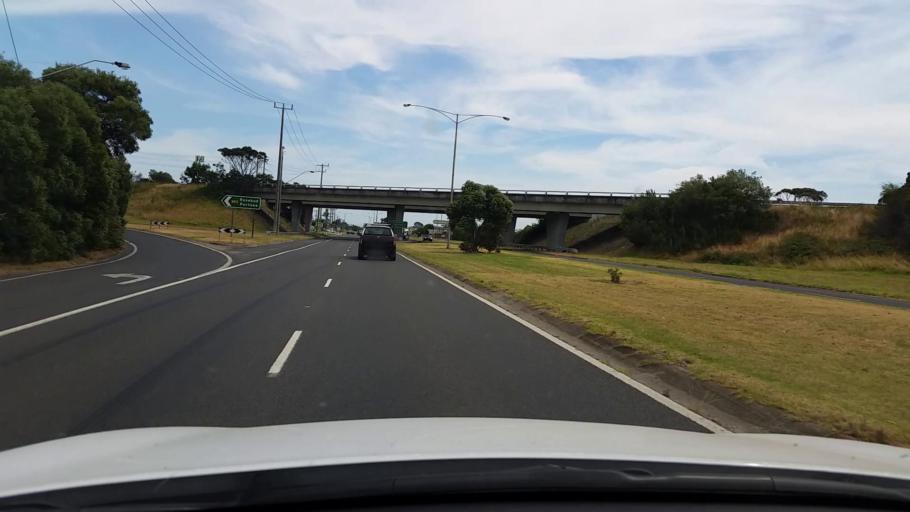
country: AU
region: Victoria
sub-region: Mornington Peninsula
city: Safety Beach
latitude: -38.3302
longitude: 144.9906
